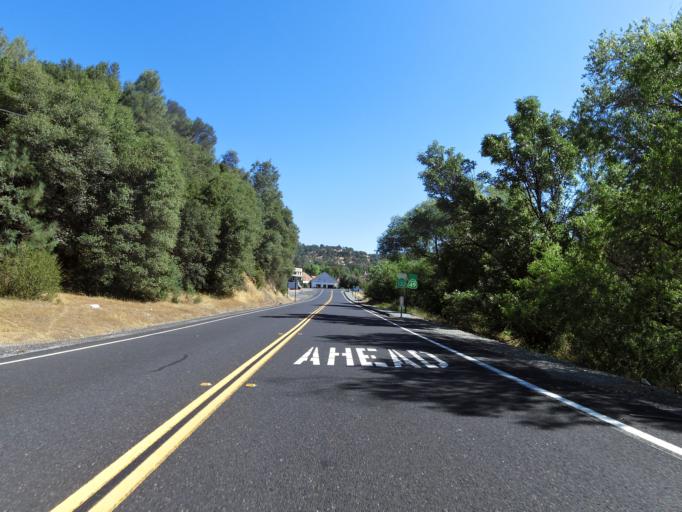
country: US
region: California
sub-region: Tuolumne County
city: Tuolumne City
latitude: 37.7083
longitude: -120.1976
